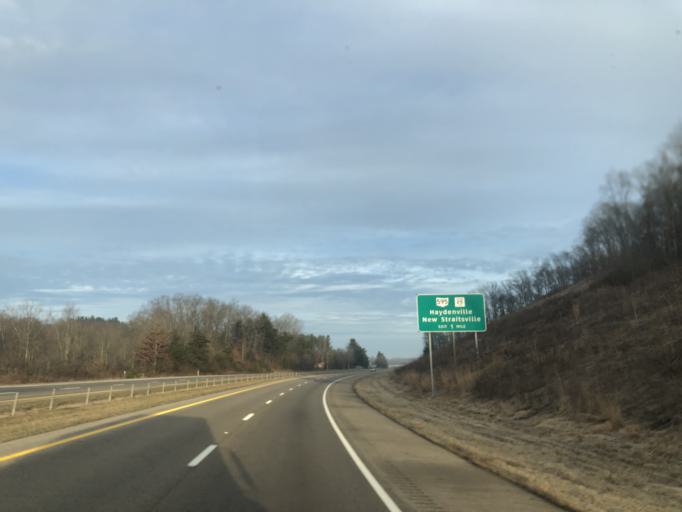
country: US
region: Ohio
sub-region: Athens County
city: Nelsonville
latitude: 39.4795
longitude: -82.3158
